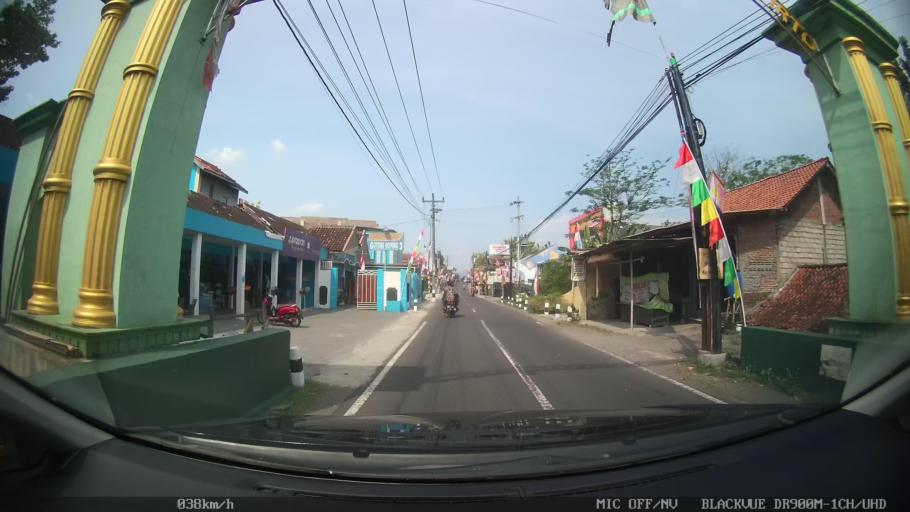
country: ID
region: Daerah Istimewa Yogyakarta
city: Depok
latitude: -7.8041
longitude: 110.4376
